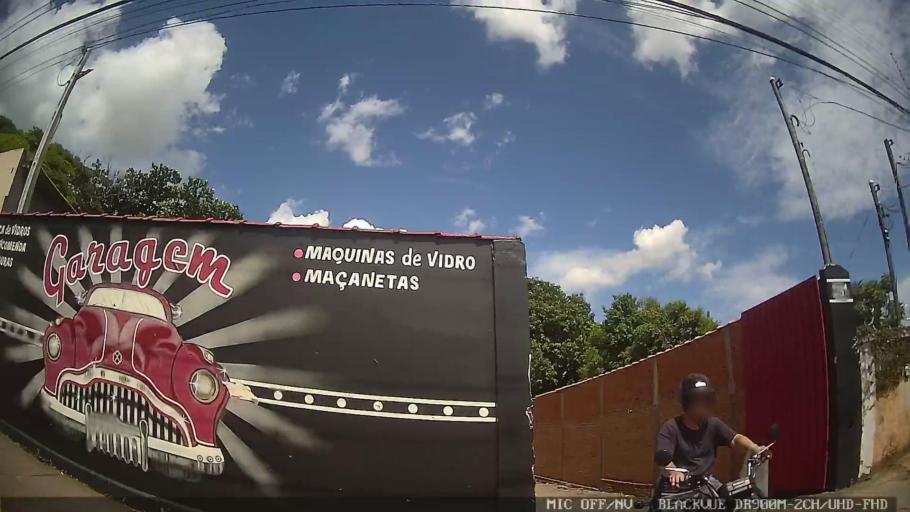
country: BR
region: Sao Paulo
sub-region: Conchas
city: Conchas
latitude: -23.0315
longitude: -48.0152
